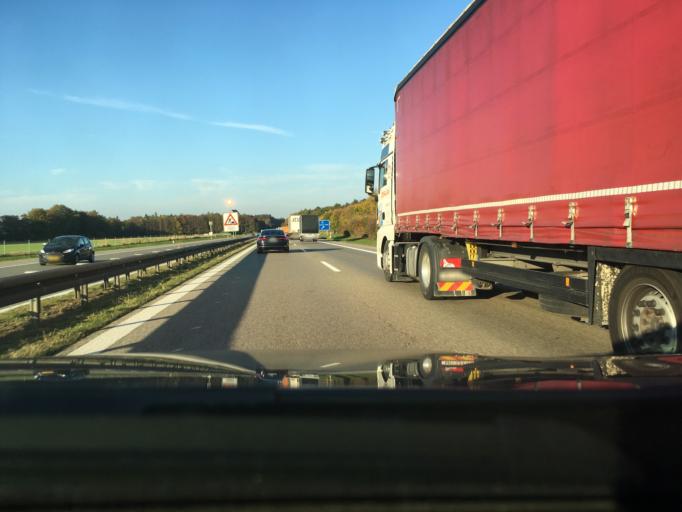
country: DE
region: Bavaria
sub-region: Swabia
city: Buxheim
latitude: 47.9670
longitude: 10.1147
